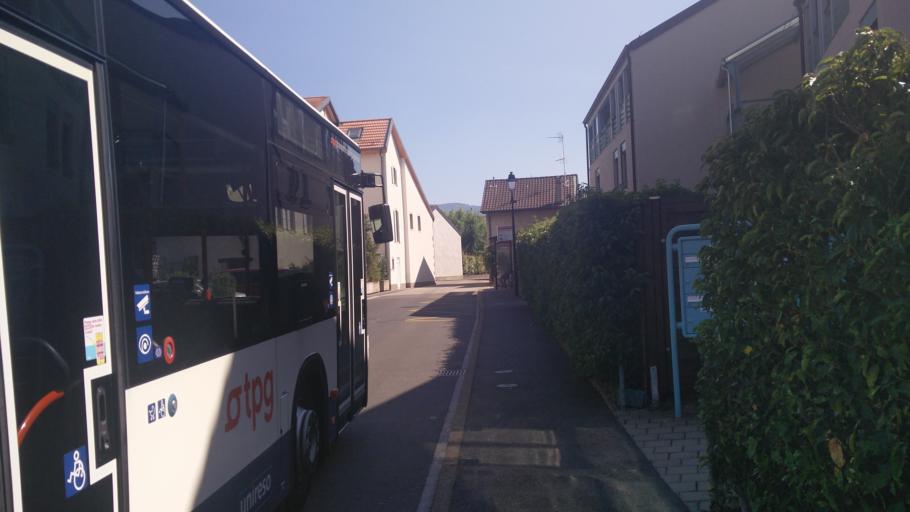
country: CH
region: Geneva
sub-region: Geneva
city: Bernex
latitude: 46.1645
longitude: 6.0562
